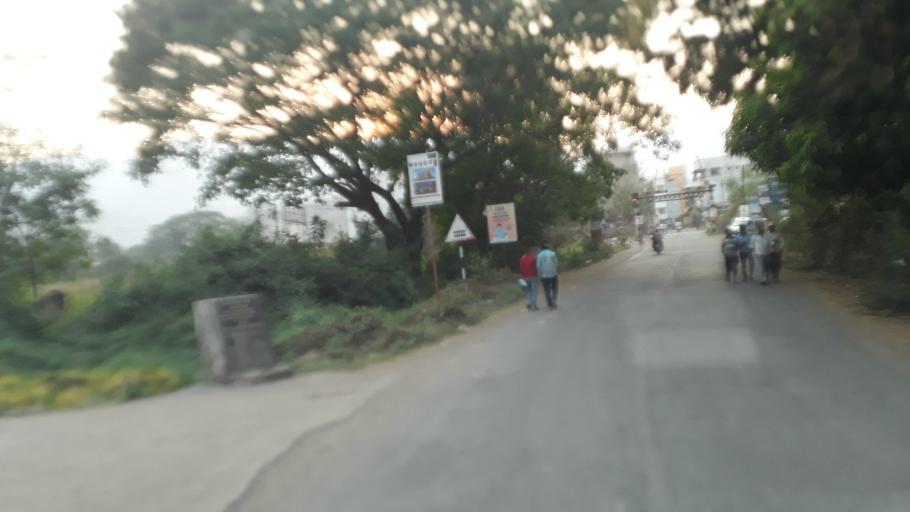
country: IN
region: Maharashtra
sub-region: Raigarh
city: Neral
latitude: 19.0223
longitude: 73.3201
